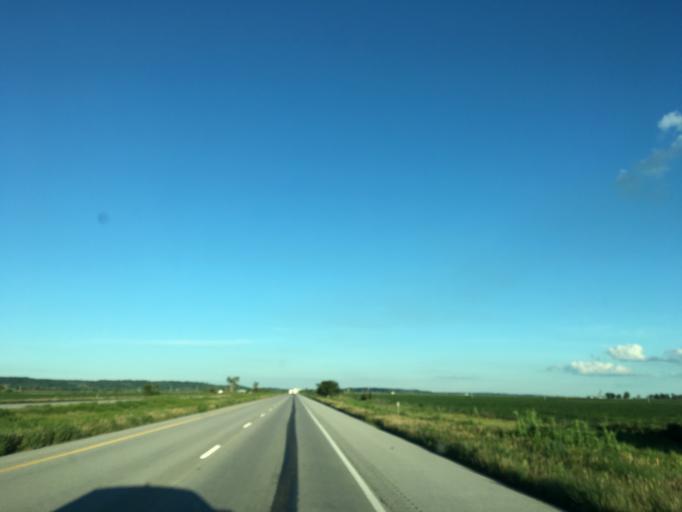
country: US
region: Iowa
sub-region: Fremont County
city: Hamburg
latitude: 40.6345
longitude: -95.7266
